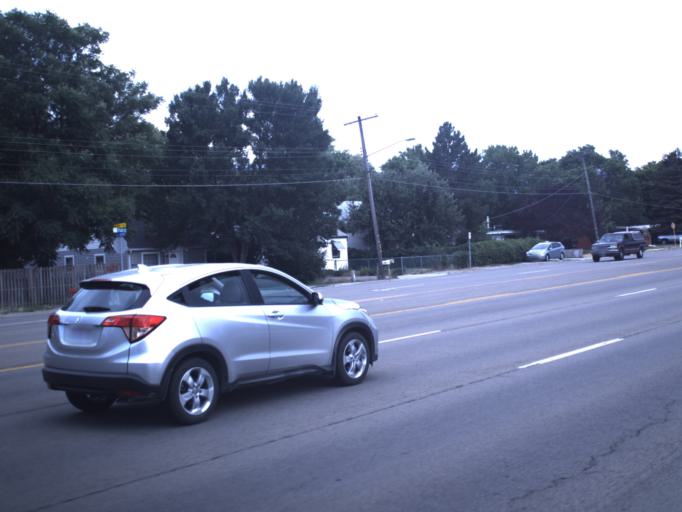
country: US
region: Utah
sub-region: Salt Lake County
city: Millcreek
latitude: 40.6914
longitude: -111.8716
